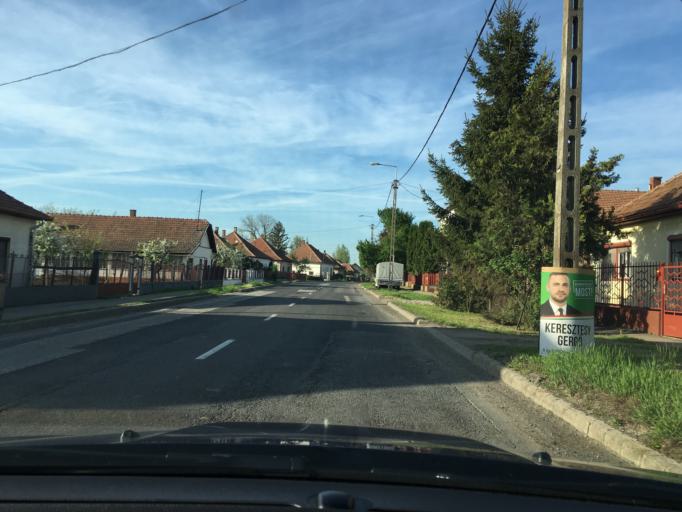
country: HU
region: Hajdu-Bihar
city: Csokmo
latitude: 47.0298
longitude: 21.2952
